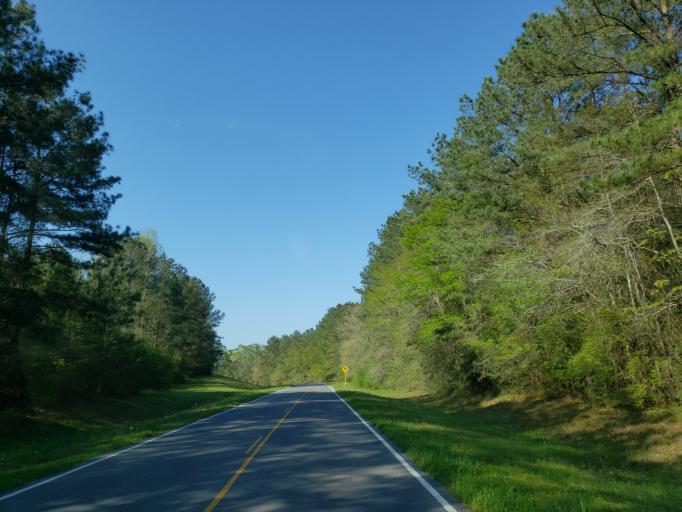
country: US
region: Mississippi
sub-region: Smith County
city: Taylorsville
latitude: 31.6844
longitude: -89.4126
